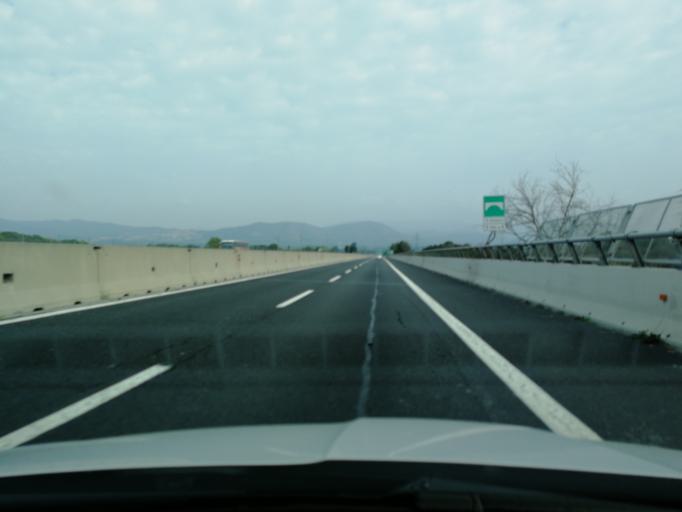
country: IT
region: Latium
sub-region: Citta metropolitana di Roma Capitale
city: Bagni di Tivoli
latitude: 41.9263
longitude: 12.7097
